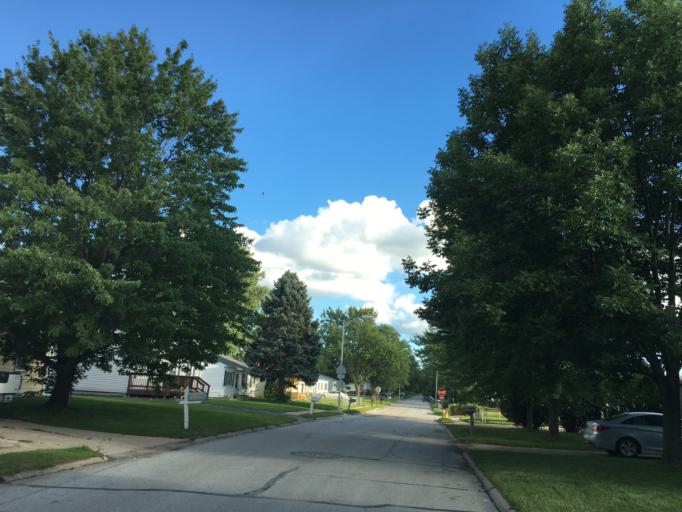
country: US
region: Nebraska
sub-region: Sarpy County
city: La Vista
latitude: 41.1827
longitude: -95.9727
